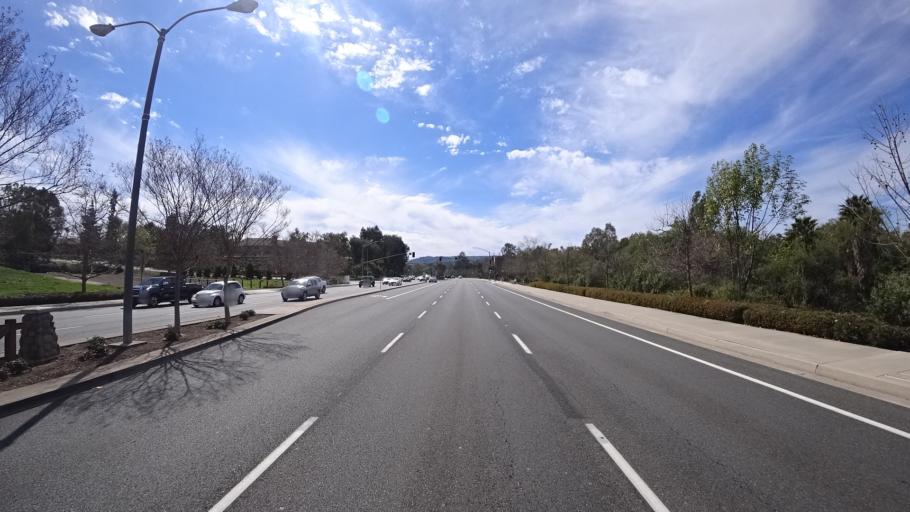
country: US
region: California
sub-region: Orange County
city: Laguna Hills
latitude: 33.5873
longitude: -117.7032
